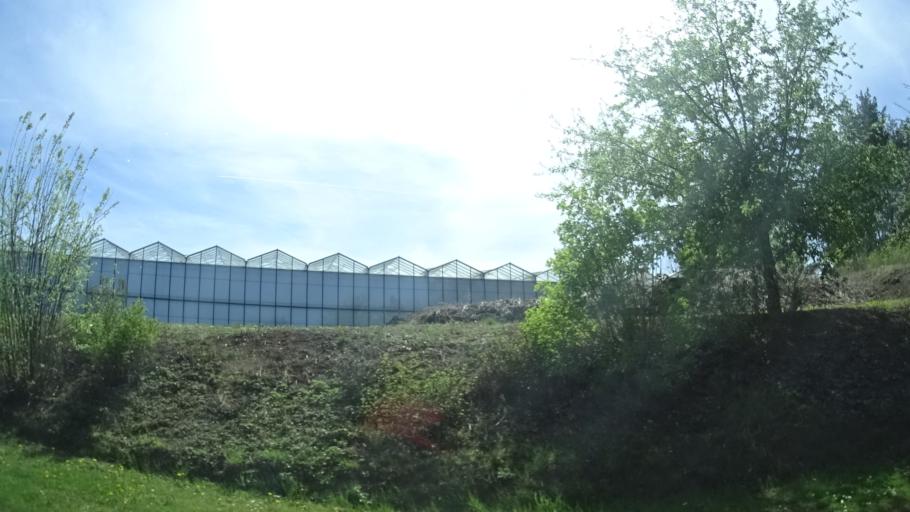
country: DE
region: Bavaria
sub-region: Regierungsbezirk Unterfranken
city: Maroldsweisach
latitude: 50.1758
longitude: 10.6294
